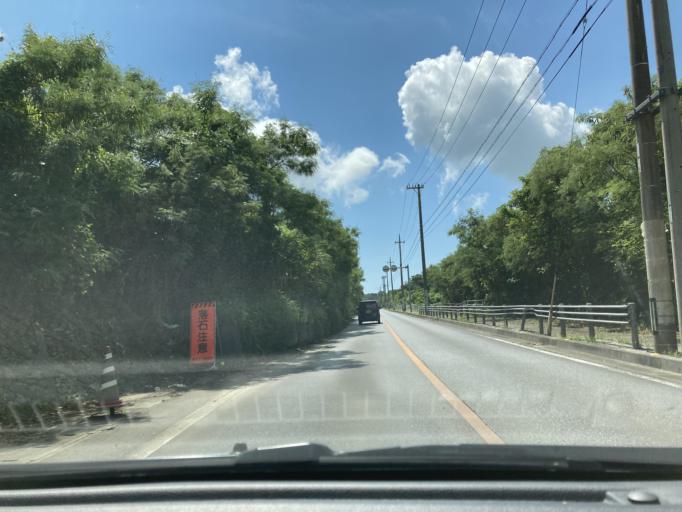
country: JP
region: Okinawa
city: Tomigusuku
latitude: 26.1599
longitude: 127.7711
